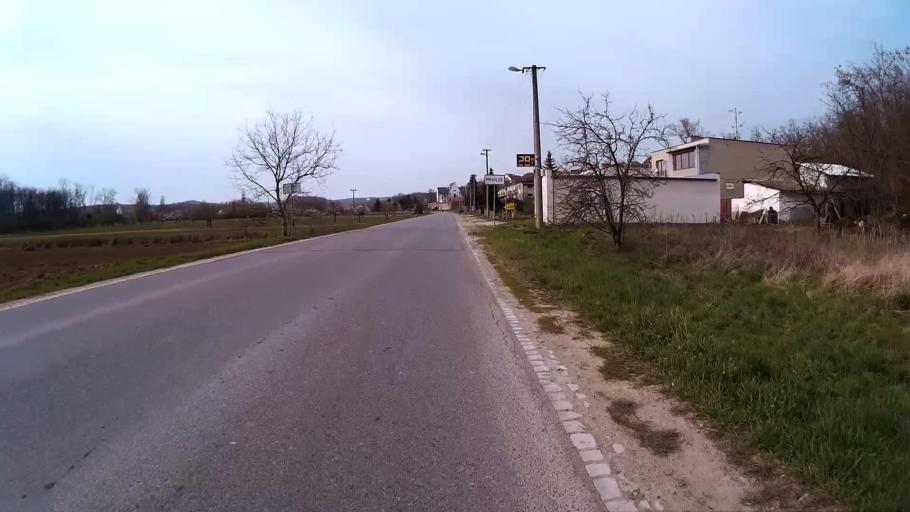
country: CZ
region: South Moravian
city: Dolni Kounice
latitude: 49.0512
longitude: 16.4916
